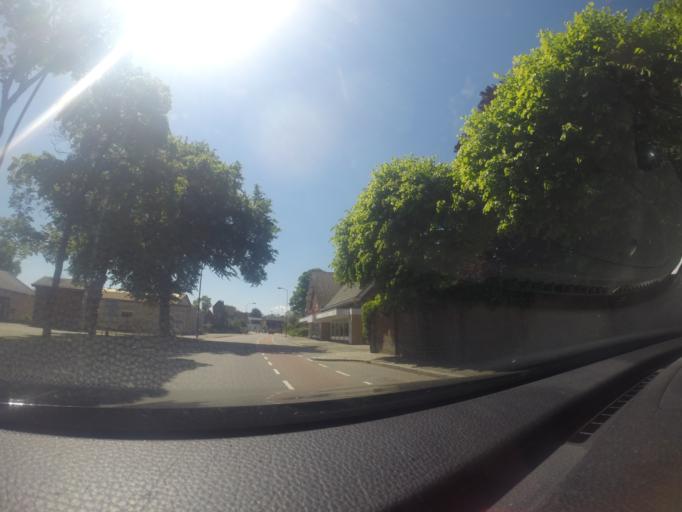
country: NL
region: Gelderland
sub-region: Gemeente Apeldoorn
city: Loenen
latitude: 52.1216
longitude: 6.0220
